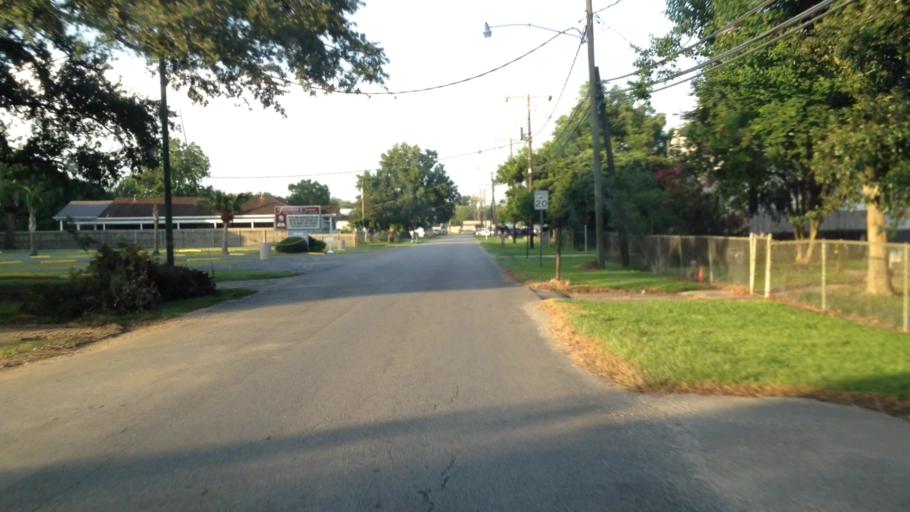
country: US
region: Louisiana
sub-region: Jefferson Parish
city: Bridge City
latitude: 29.9324
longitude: -90.1590
